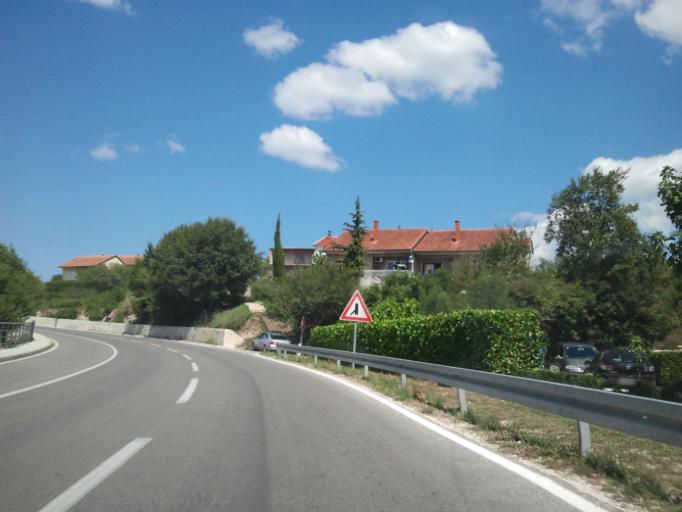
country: HR
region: Zadarska
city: Benkovac
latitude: 44.0371
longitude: 15.6201
